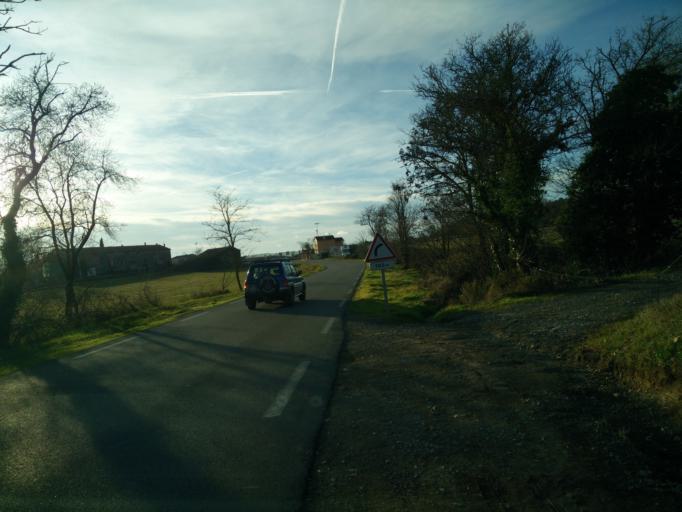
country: FR
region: Provence-Alpes-Cote d'Azur
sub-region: Departement du Var
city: Callian
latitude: 43.6110
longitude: 6.7356
